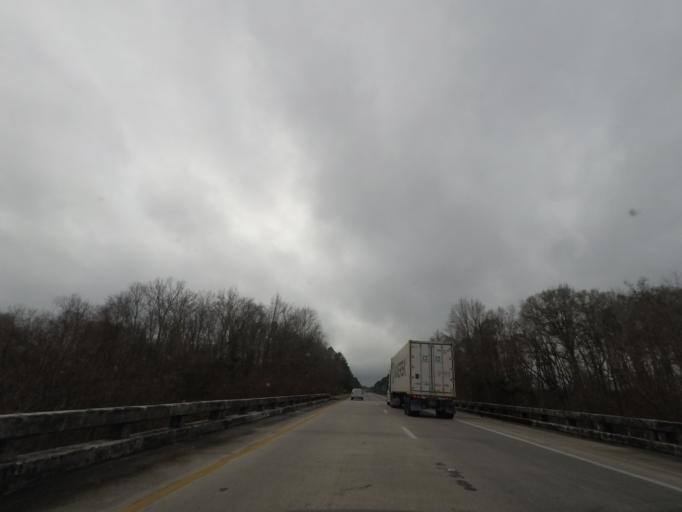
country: US
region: South Carolina
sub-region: Orangeburg County
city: Holly Hill
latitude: 33.3391
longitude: -80.5363
